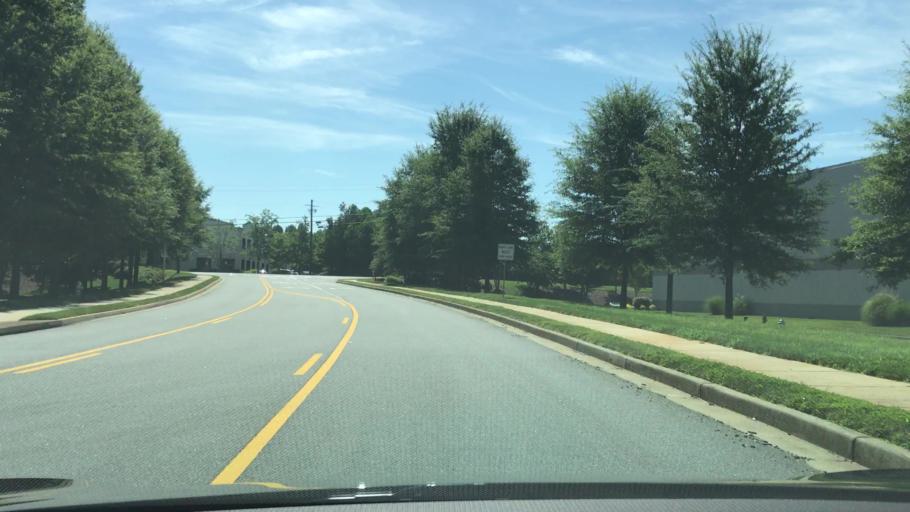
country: US
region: Georgia
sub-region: Gwinnett County
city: Suwanee
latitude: 34.0635
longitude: -84.0653
